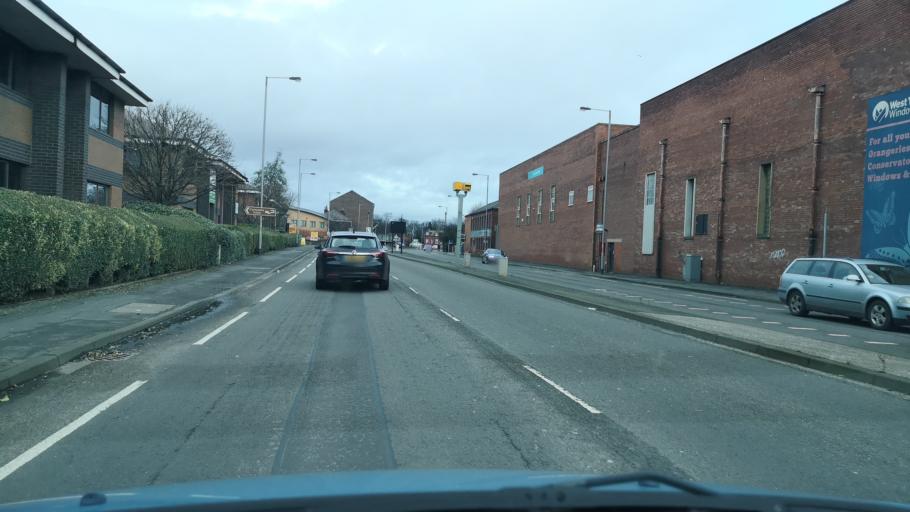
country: GB
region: England
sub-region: City and Borough of Wakefield
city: Wakefield
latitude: 53.6664
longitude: -1.5063
